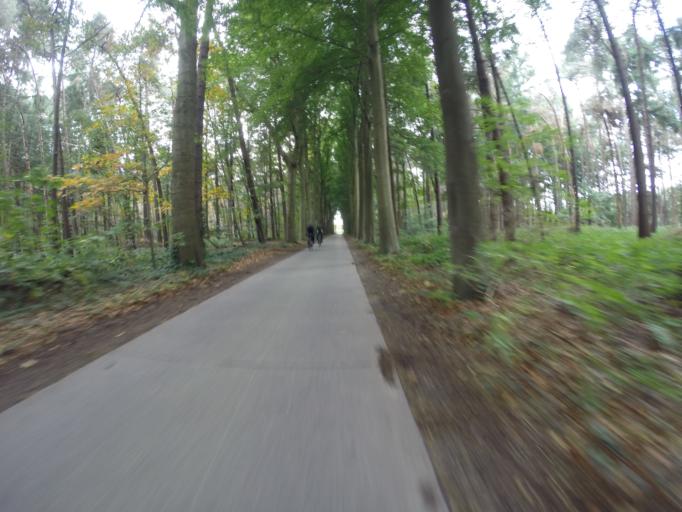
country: BE
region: Flanders
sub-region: Provincie West-Vlaanderen
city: Ruiselede
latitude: 51.0877
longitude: 3.3690
